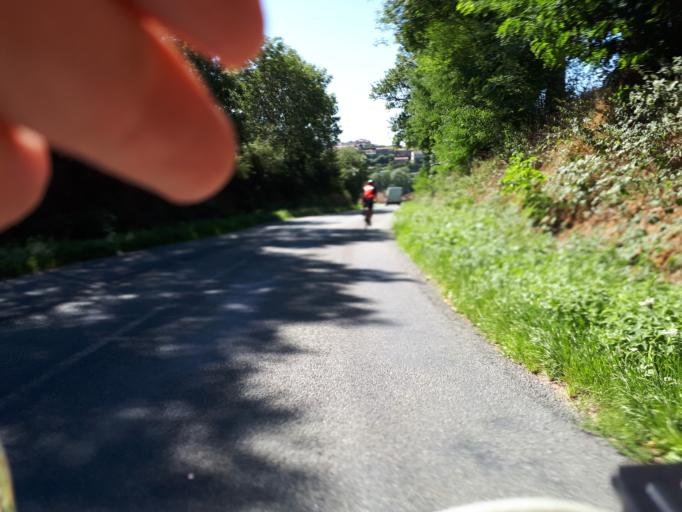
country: FR
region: Rhone-Alpes
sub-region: Departement de la Loire
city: Panissieres
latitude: 45.8003
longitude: 4.3399
